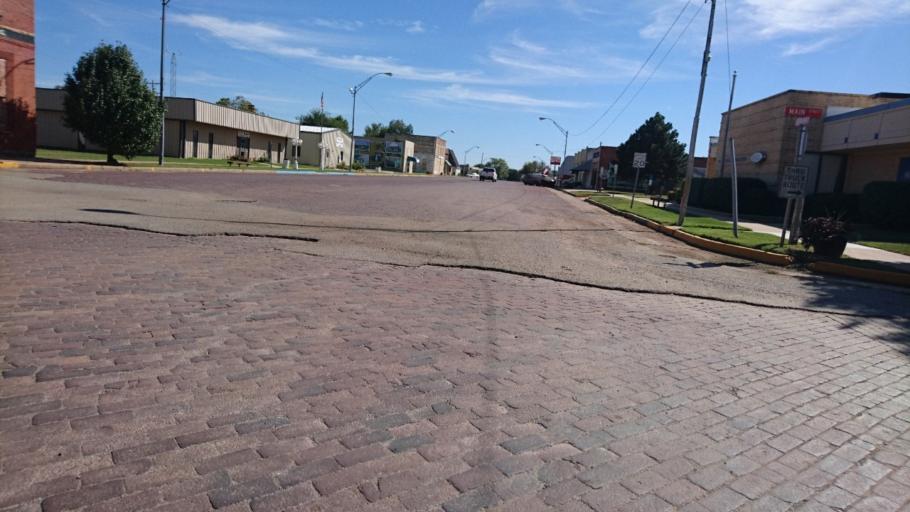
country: US
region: Oklahoma
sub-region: Lincoln County
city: Stroud
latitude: 35.7059
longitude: -96.7653
